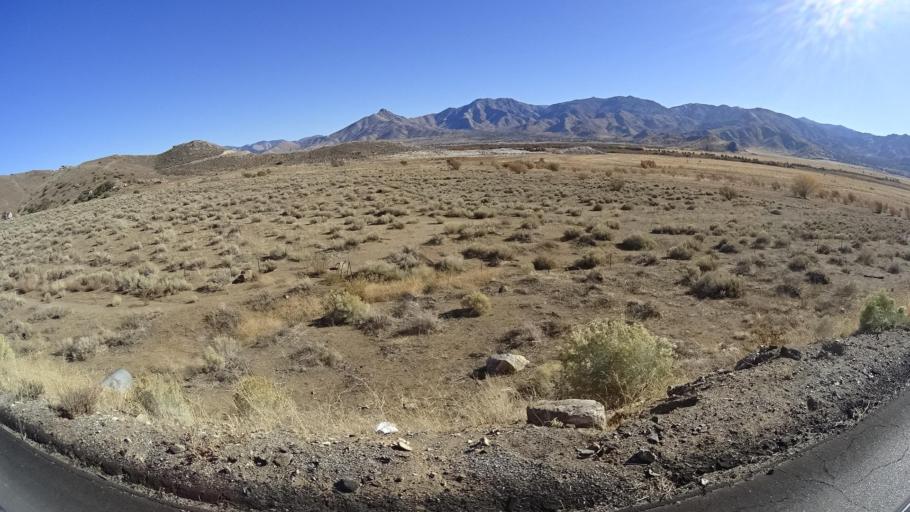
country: US
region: California
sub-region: Kern County
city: Wofford Heights
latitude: 35.6775
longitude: -118.3981
